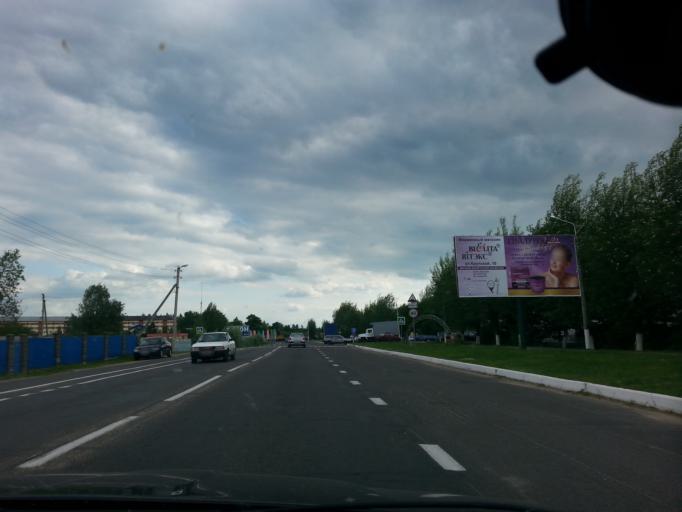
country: BY
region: Minsk
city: Myadzyel
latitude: 54.8697
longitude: 26.9357
